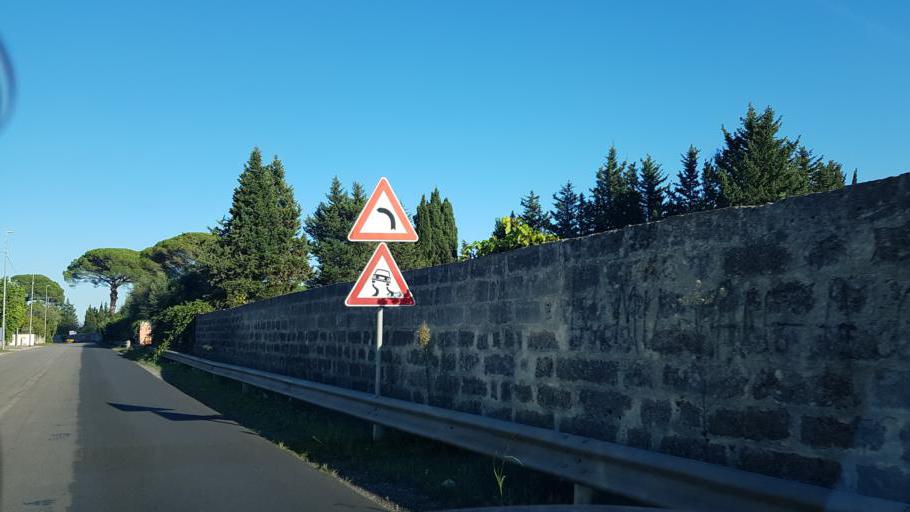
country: IT
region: Apulia
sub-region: Provincia di Lecce
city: Arnesano
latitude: 40.3339
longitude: 18.0980
